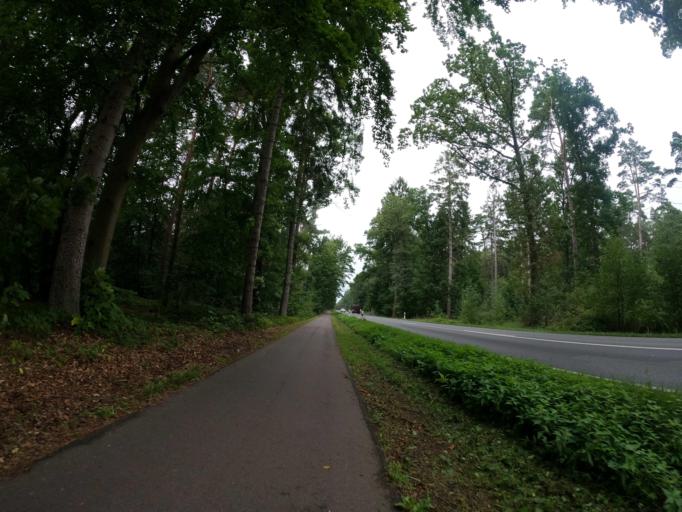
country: DE
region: Mecklenburg-Vorpommern
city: Ostseebad Gohren
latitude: 54.3456
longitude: 13.7080
